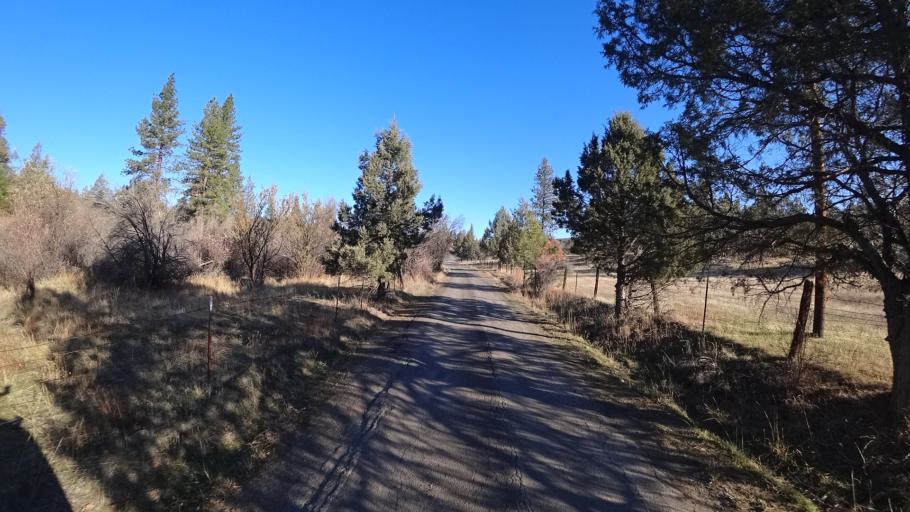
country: US
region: Oregon
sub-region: Jackson County
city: Ashland
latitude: 41.9839
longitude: -122.6233
